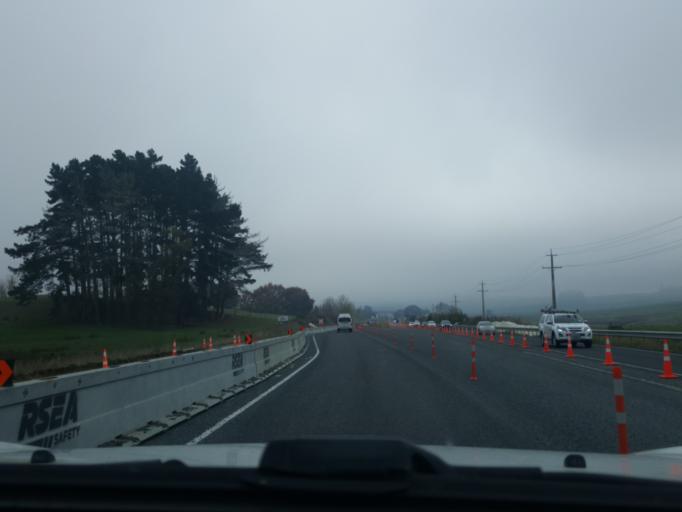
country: NZ
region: Waikato
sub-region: Waikato District
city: Te Kauwhata
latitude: -37.3626
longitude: 175.0894
